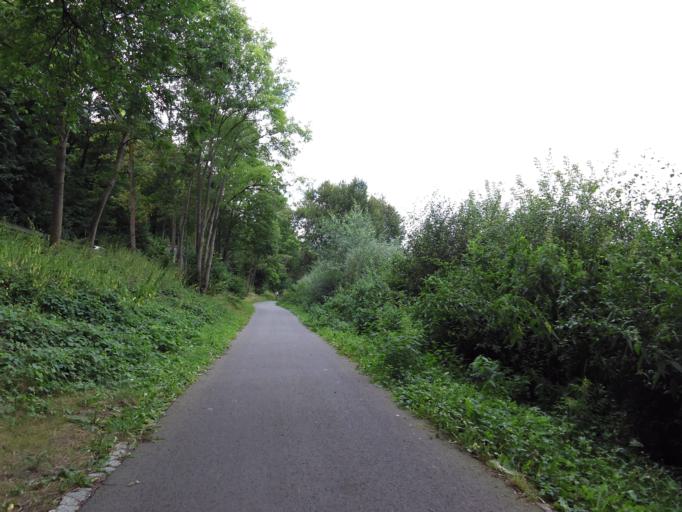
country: DE
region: Saxony
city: Meissen
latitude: 51.1377
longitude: 13.5021
